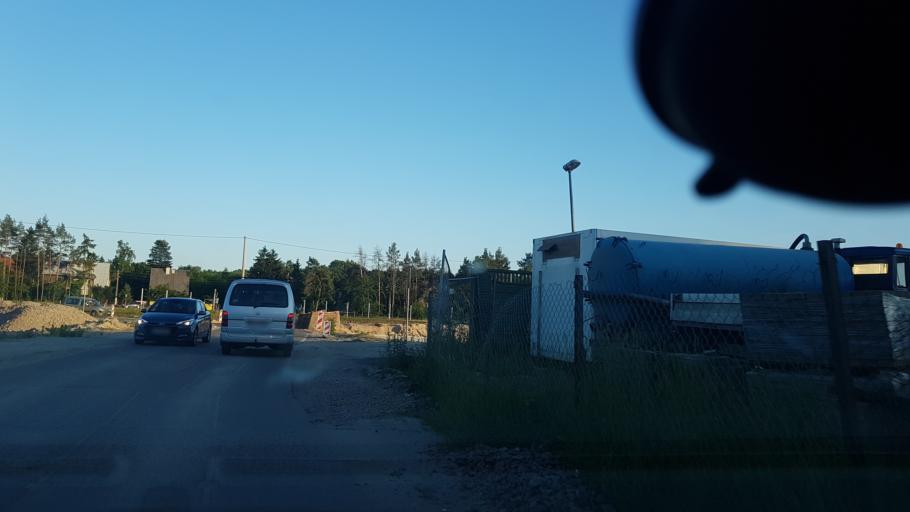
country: PL
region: Masovian Voivodeship
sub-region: Warszawa
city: Wawer
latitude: 52.1702
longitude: 21.2081
